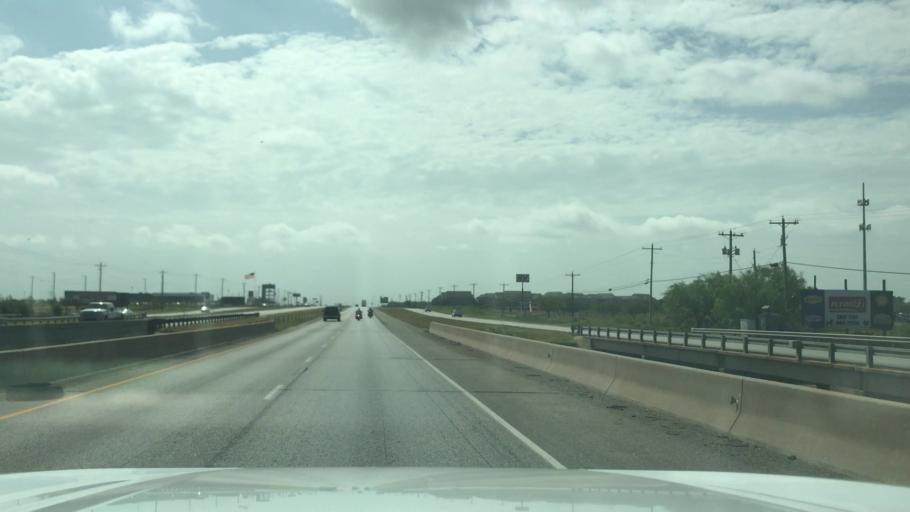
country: US
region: Texas
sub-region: Taylor County
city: Abilene
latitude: 32.4870
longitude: -99.7148
